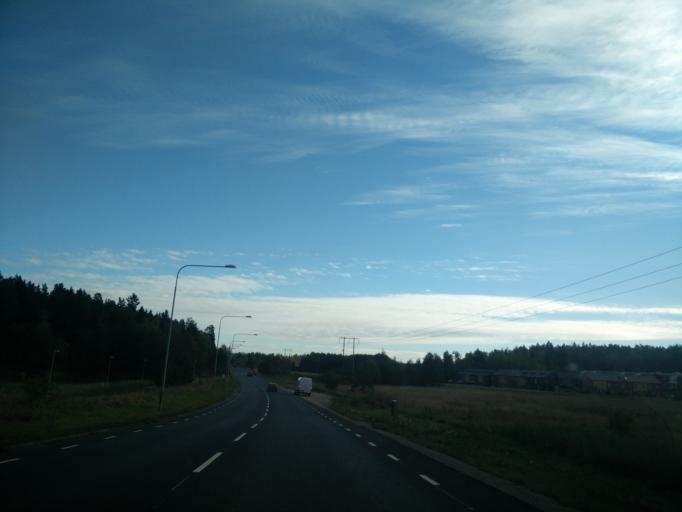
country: SE
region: Stockholm
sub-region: Upplands Vasby Kommun
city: Upplands Vaesby
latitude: 59.5111
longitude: 17.9526
